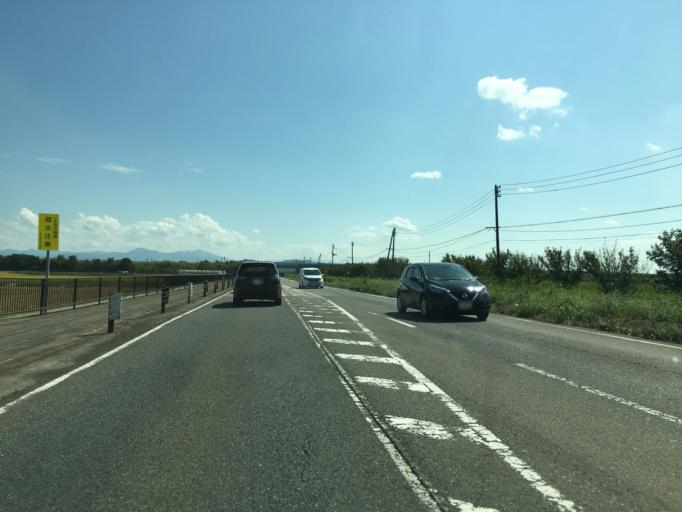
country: JP
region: Niigata
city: Niitsu-honcho
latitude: 37.8247
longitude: 139.0983
